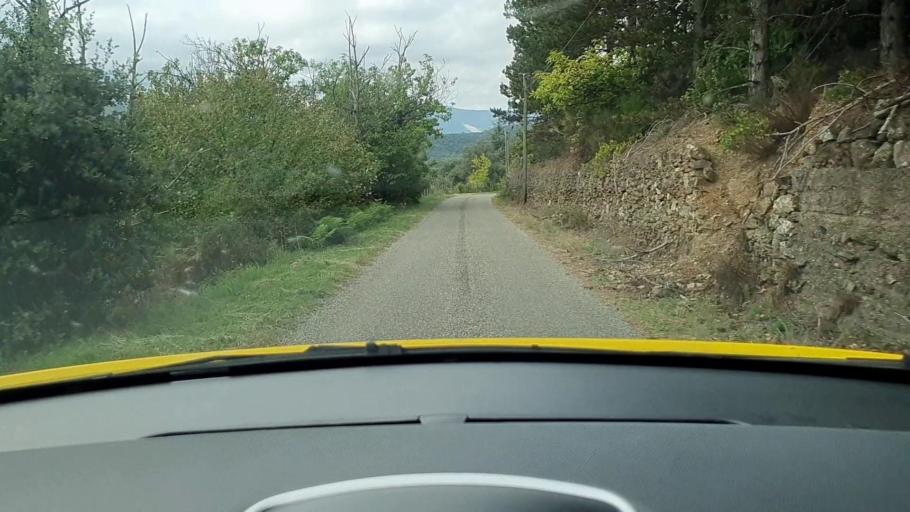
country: FR
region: Languedoc-Roussillon
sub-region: Departement du Gard
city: Sumene
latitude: 44.0168
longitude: 3.6679
